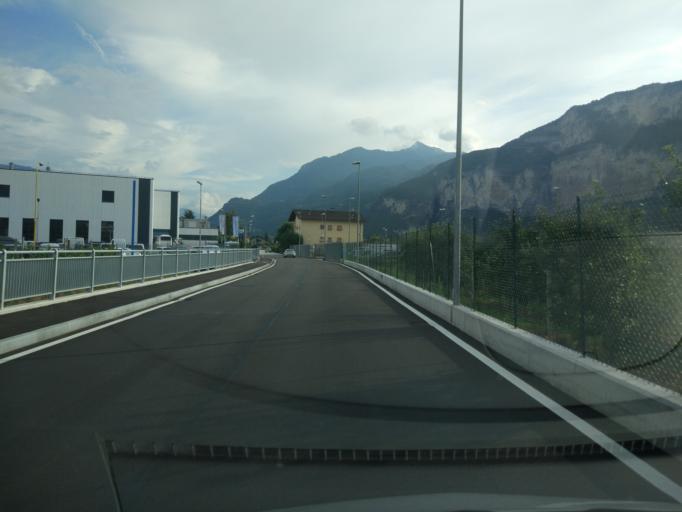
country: IT
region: Trentino-Alto Adige
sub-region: Provincia di Trento
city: Meano
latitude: 46.1119
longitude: 11.1057
